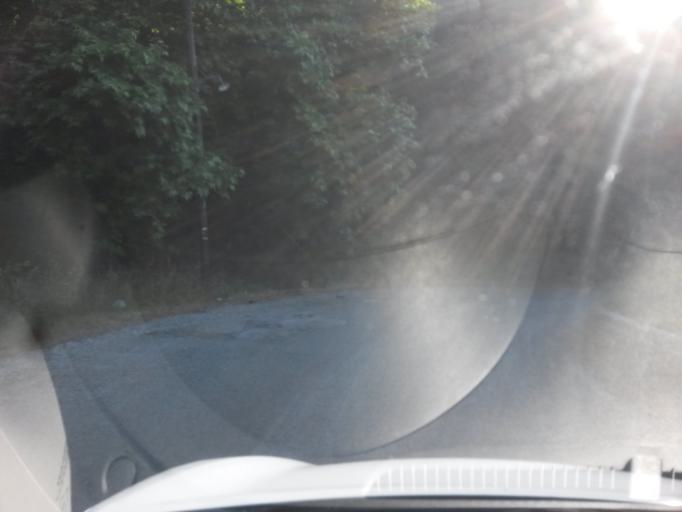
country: GR
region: North Aegean
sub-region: Nomos Lesvou
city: Mantamados
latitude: 39.3599
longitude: 26.2999
